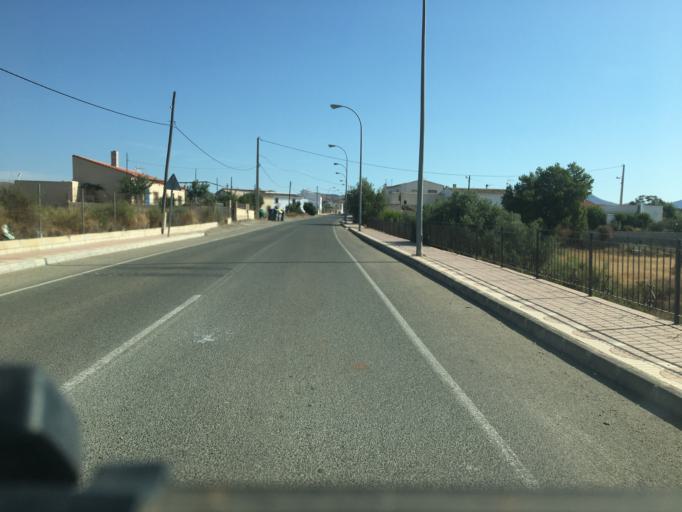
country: ES
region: Andalusia
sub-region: Provincia de Almeria
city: Huercal-Overa
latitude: 37.4644
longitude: -1.9876
